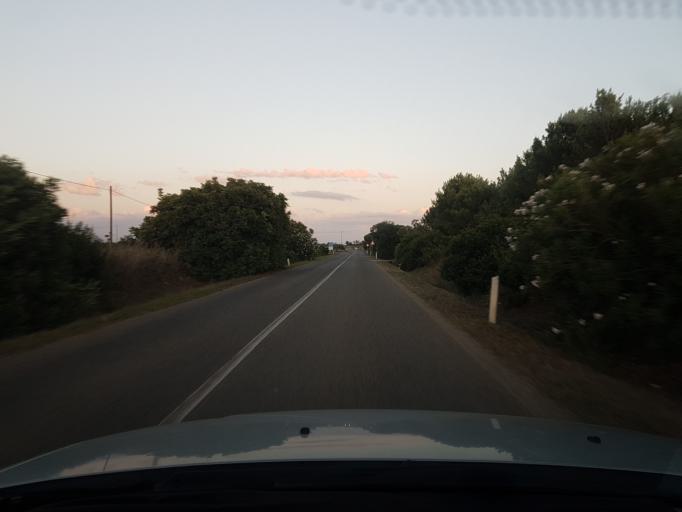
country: IT
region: Sardinia
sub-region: Provincia di Oristano
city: Riola Sardo
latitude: 40.0269
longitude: 8.4280
